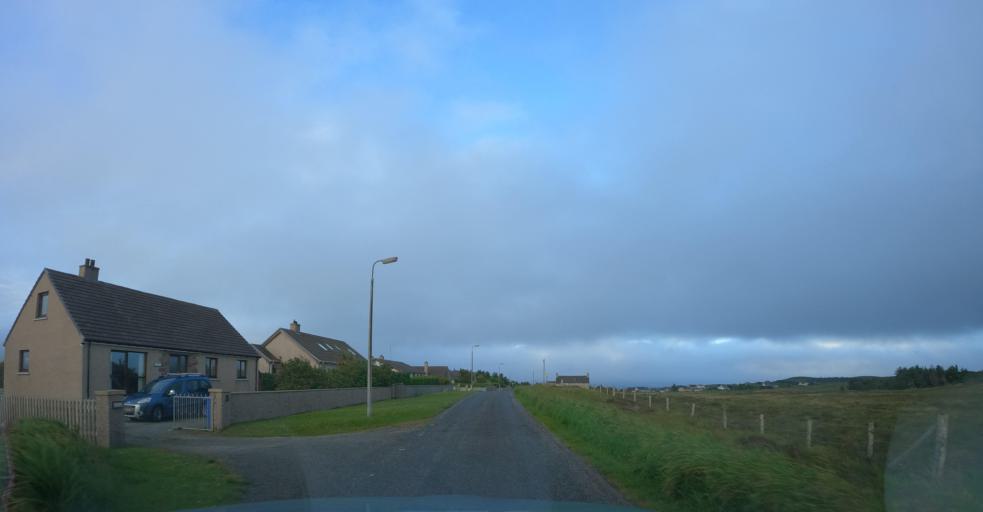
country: GB
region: Scotland
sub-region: Eilean Siar
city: Stornoway
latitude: 58.2020
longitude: -6.2318
